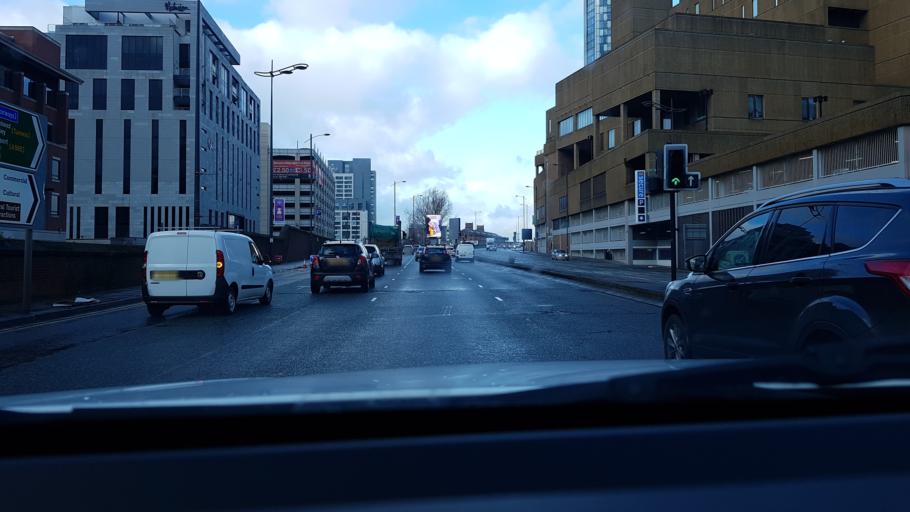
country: GB
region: England
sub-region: Liverpool
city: Liverpool
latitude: 53.4075
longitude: -2.9960
